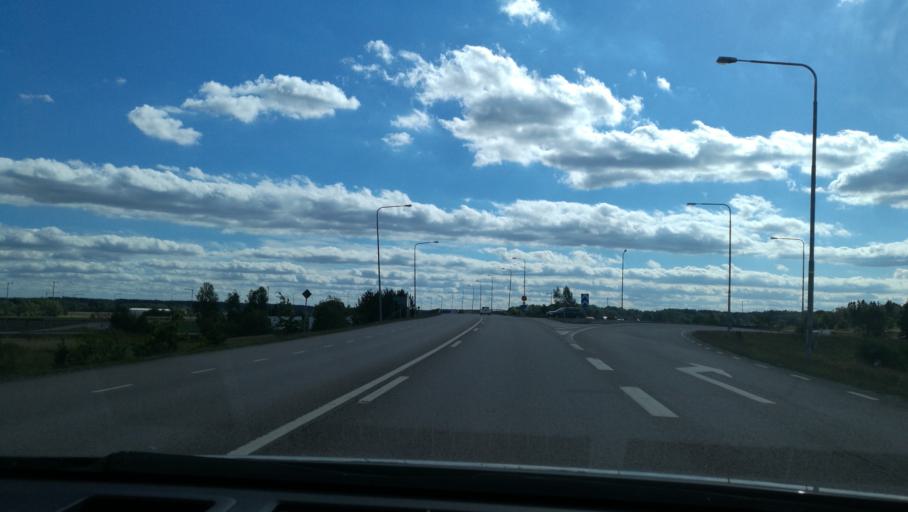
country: SE
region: Vaestra Goetaland
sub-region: Mariestads Kommun
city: Mariestad
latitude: 58.6768
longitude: 13.8164
